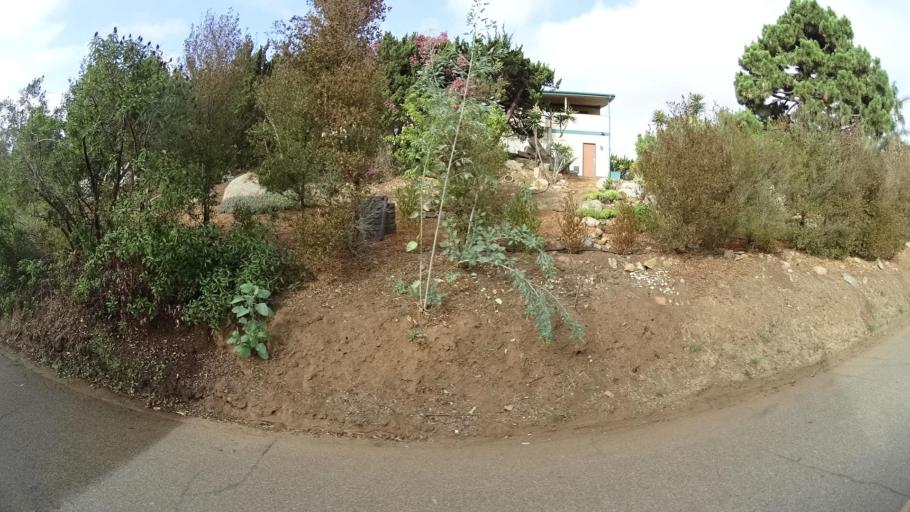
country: US
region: California
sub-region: San Diego County
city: Vista
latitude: 33.2004
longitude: -117.2086
